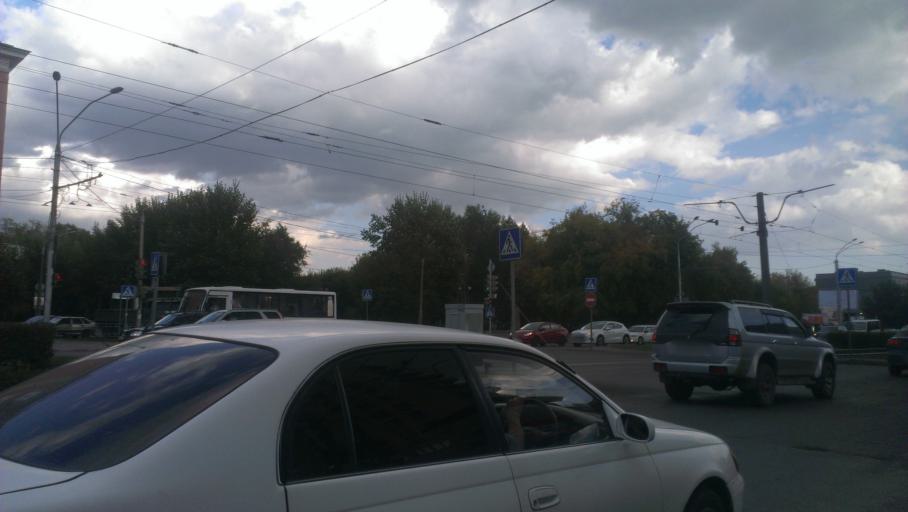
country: RU
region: Altai Krai
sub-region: Gorod Barnaulskiy
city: Barnaul
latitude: 53.3581
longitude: 83.7662
